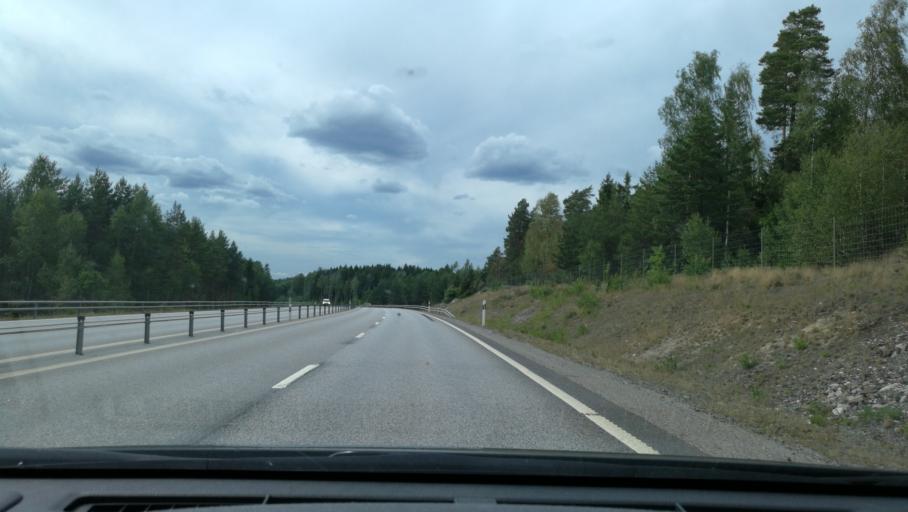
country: SE
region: OEstergoetland
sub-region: Norrkopings Kommun
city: Svartinge
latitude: 58.6701
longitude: 15.9938
